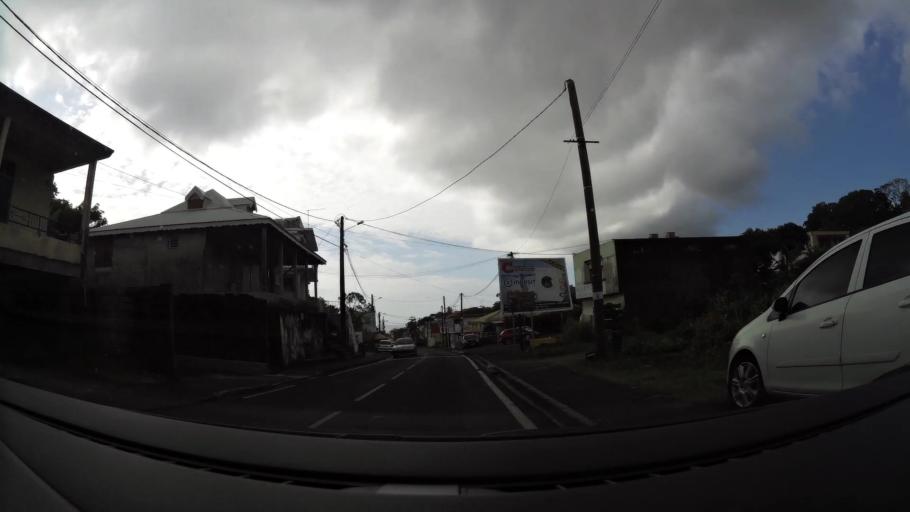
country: GP
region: Guadeloupe
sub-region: Guadeloupe
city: Trois-Rivieres
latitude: 15.9776
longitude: -61.6406
